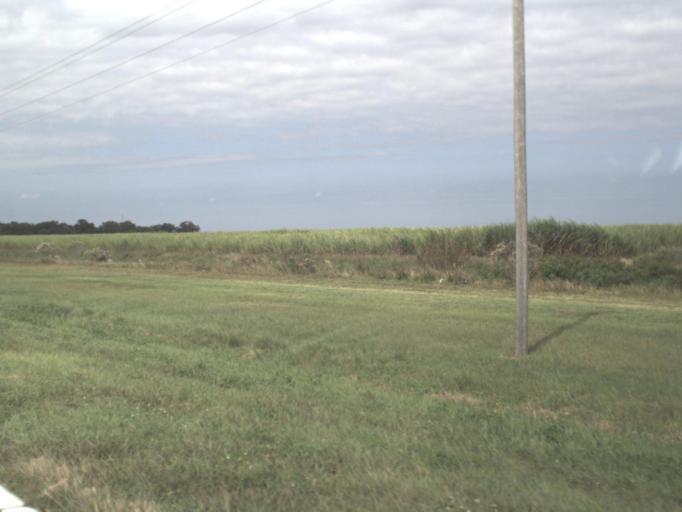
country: US
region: Florida
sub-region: Glades County
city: Moore Haven
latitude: 26.7527
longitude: -81.1370
